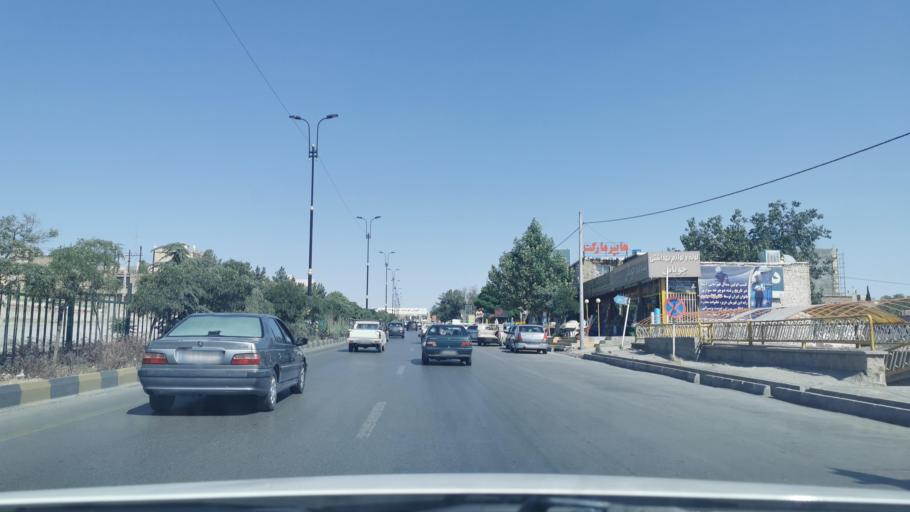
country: IR
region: Razavi Khorasan
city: Torqabeh
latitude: 36.3994
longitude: 59.3915
